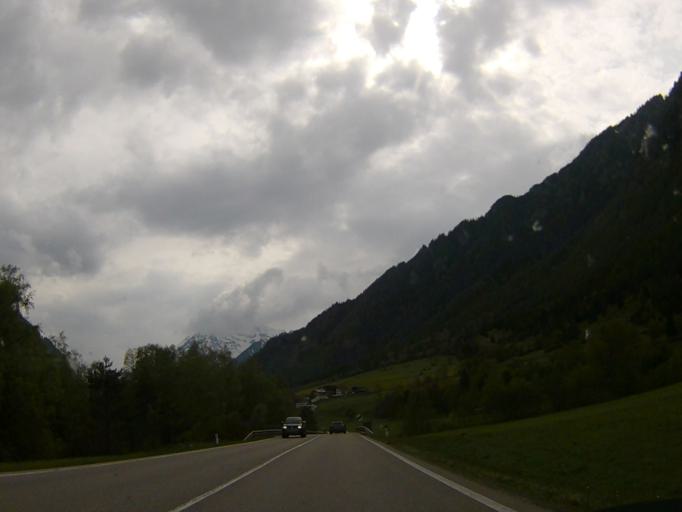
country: AT
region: Tyrol
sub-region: Politischer Bezirk Landeck
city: Pfunds
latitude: 46.9876
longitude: 10.5694
